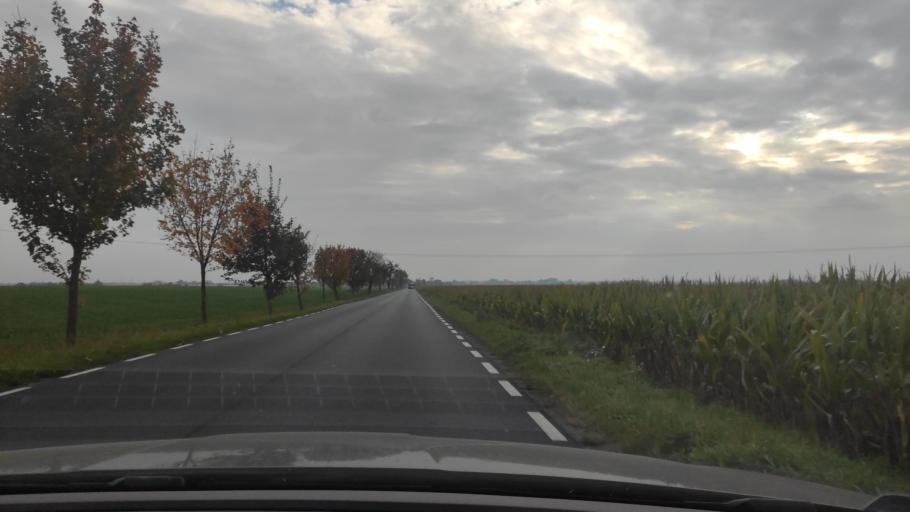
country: PL
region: Greater Poland Voivodeship
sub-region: Powiat poznanski
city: Kostrzyn
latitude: 52.4394
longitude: 17.1665
